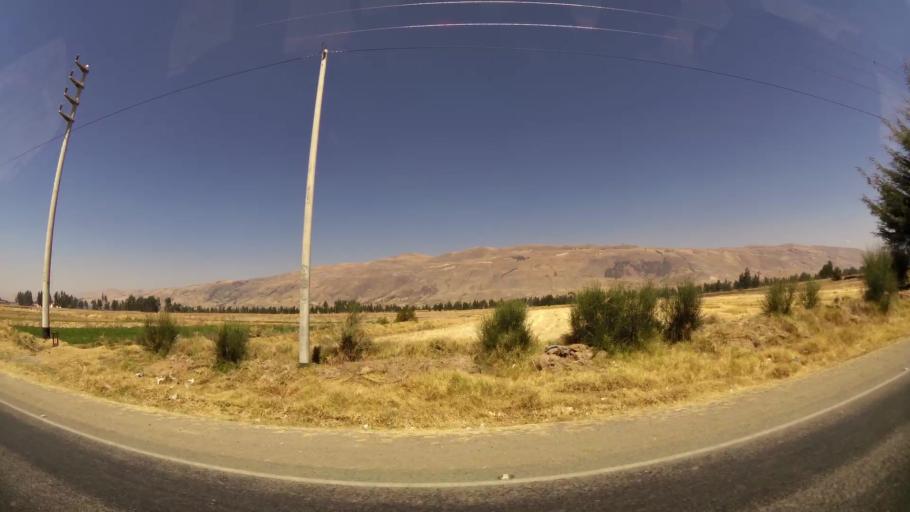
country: PE
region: Junin
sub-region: Provincia de Jauja
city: Huamali
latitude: -11.8237
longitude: -75.4105
